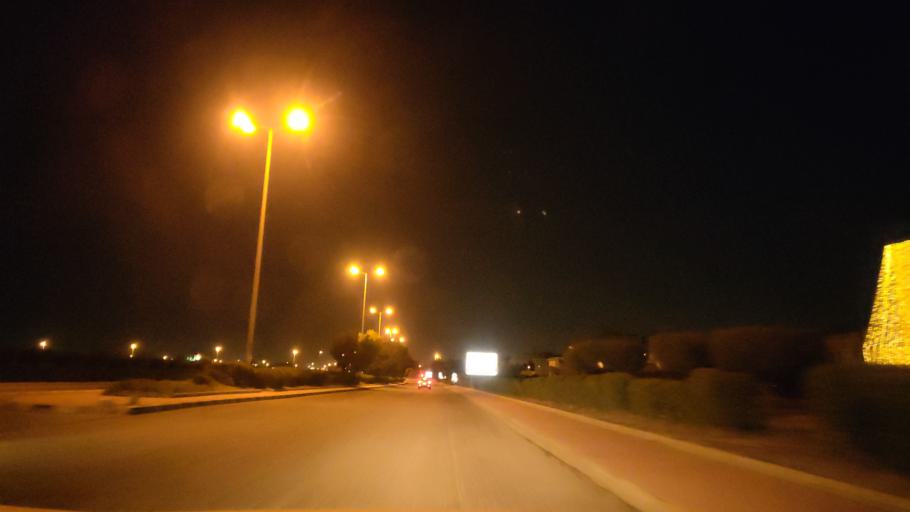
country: KW
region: Al Asimah
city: Ar Rabiyah
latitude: 29.2839
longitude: 47.9279
